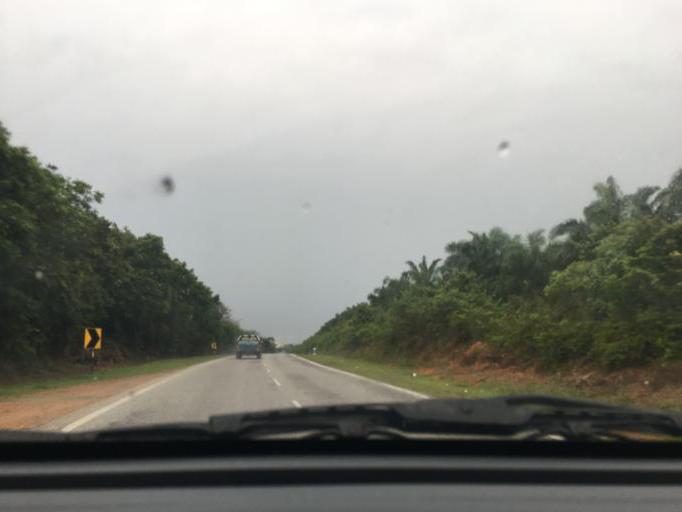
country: MY
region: Kedah
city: Sungai Petani
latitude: 5.6210
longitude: 100.6384
